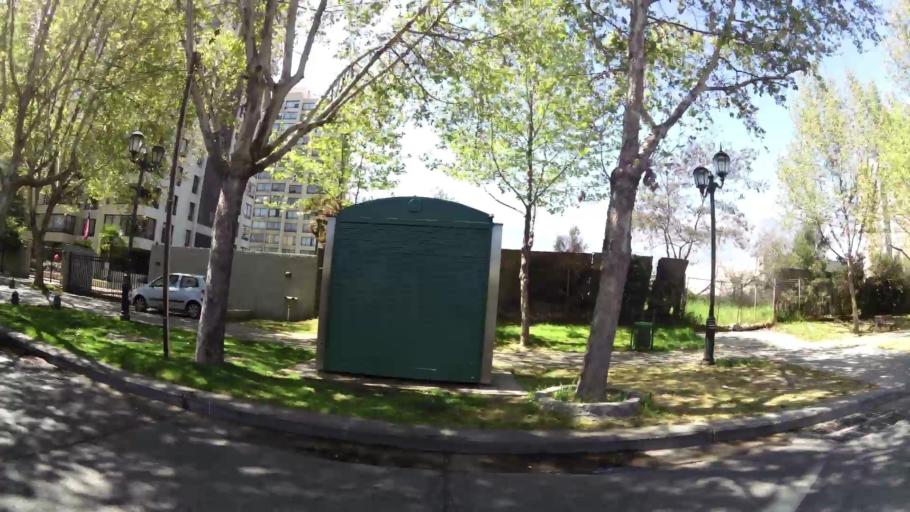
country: CL
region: Santiago Metropolitan
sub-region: Provincia de Santiago
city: Villa Presidente Frei, Nunoa, Santiago, Chile
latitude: -33.4222
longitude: -70.5401
